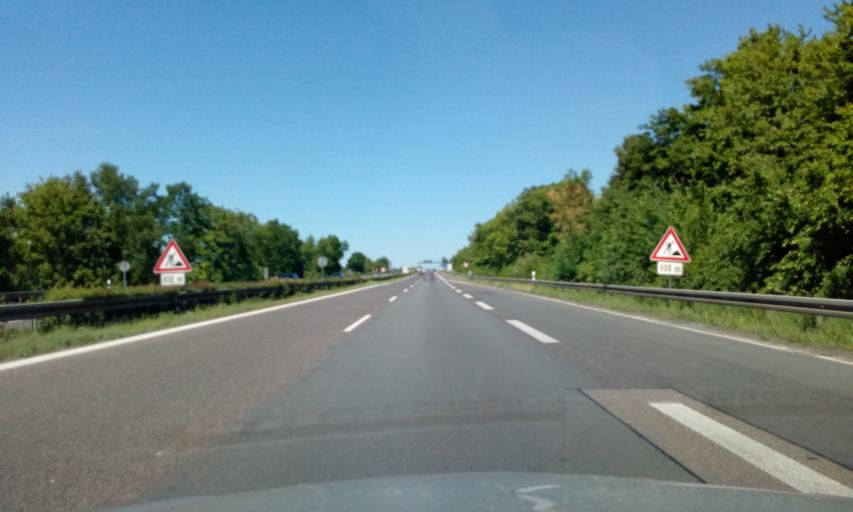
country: DE
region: North Rhine-Westphalia
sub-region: Regierungsbezirk Koln
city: Gremberghoven
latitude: 50.9122
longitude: 7.0659
